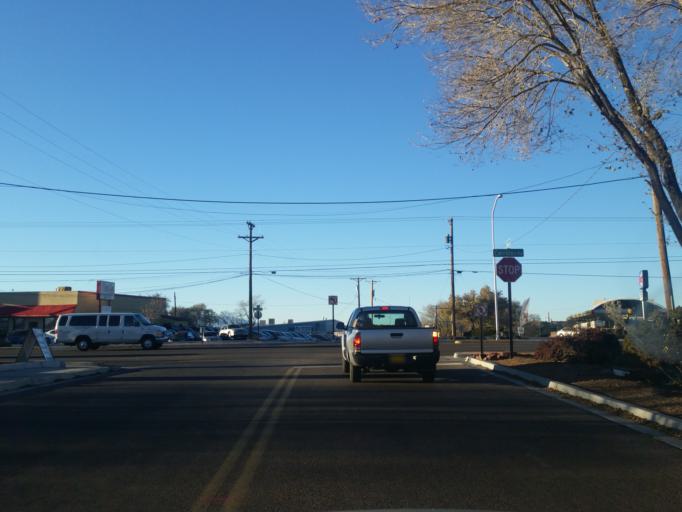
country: US
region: New Mexico
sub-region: Santa Fe County
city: Agua Fria
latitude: 35.6561
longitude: -105.9892
